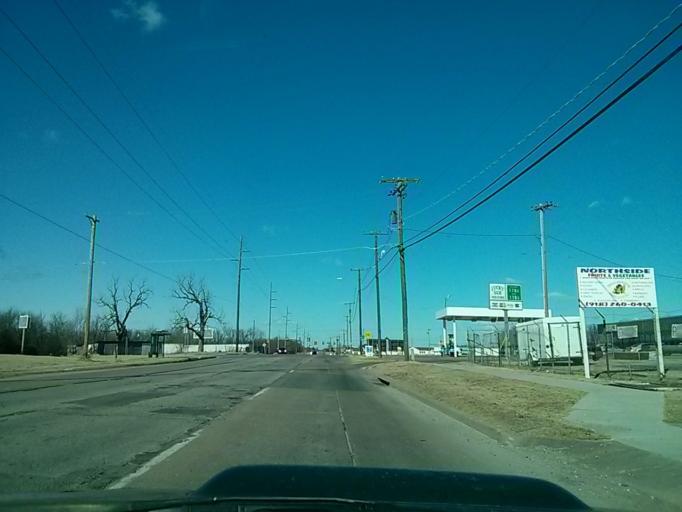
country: US
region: Oklahoma
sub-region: Tulsa County
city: Turley
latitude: 36.2039
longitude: -95.9582
